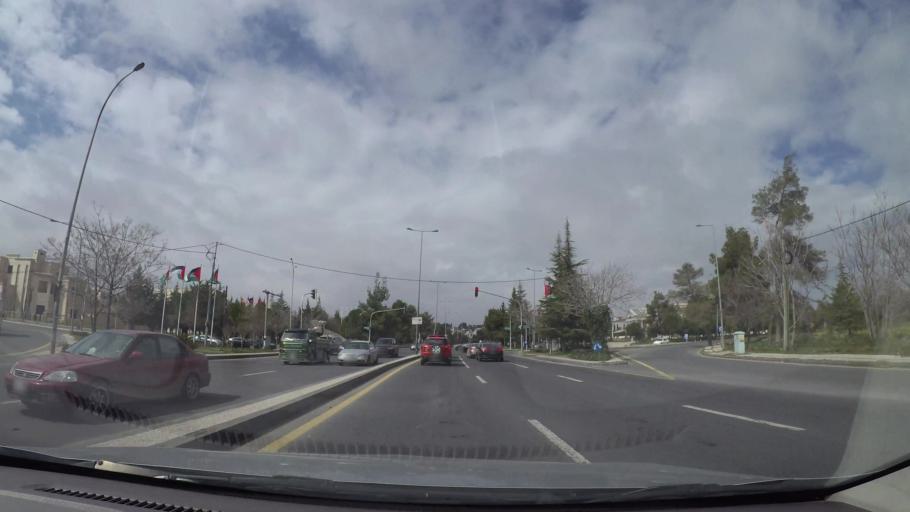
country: JO
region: Amman
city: Wadi as Sir
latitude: 31.9941
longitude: 35.8183
